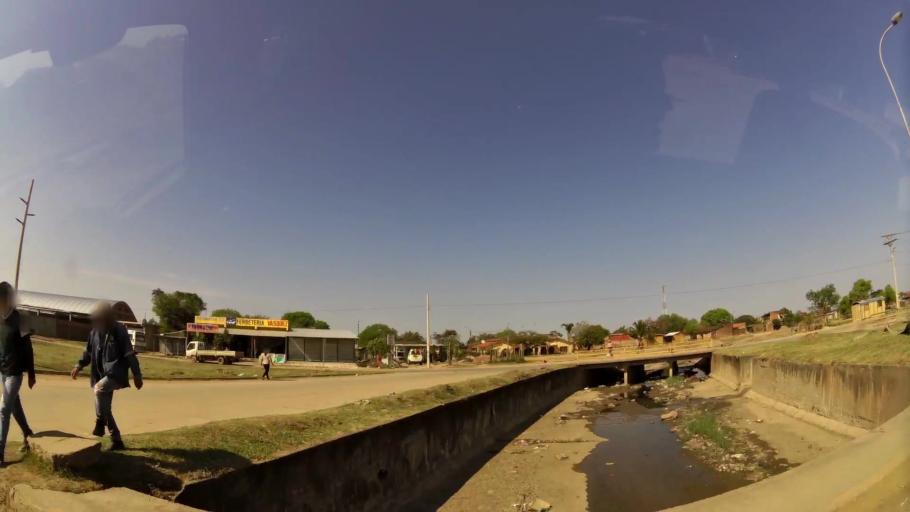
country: BO
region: Santa Cruz
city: Cotoca
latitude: -17.7780
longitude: -63.1074
